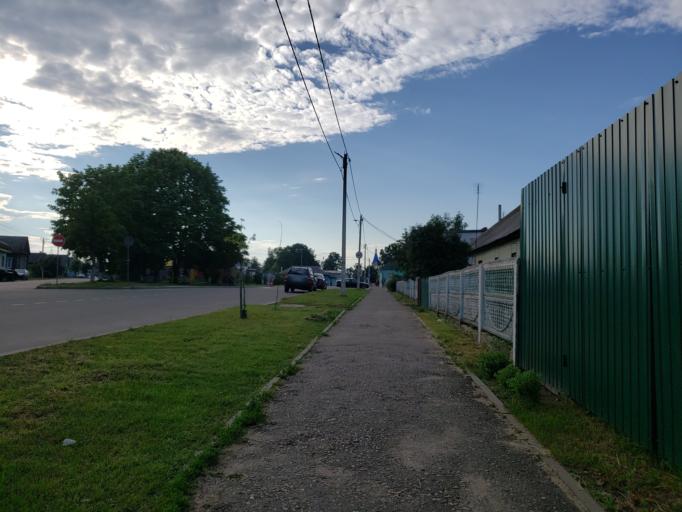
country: BY
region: Minsk
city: Chervyen'
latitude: 53.7097
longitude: 28.4274
